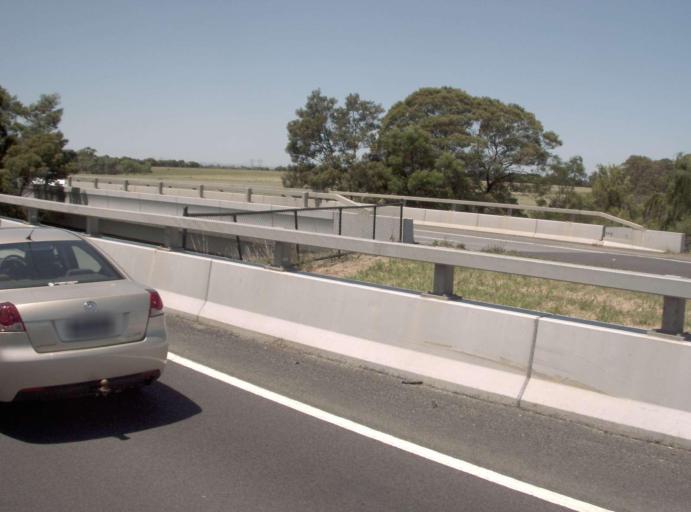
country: AU
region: Victoria
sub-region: Cardinia
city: Officer South
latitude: -38.0862
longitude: 145.4526
